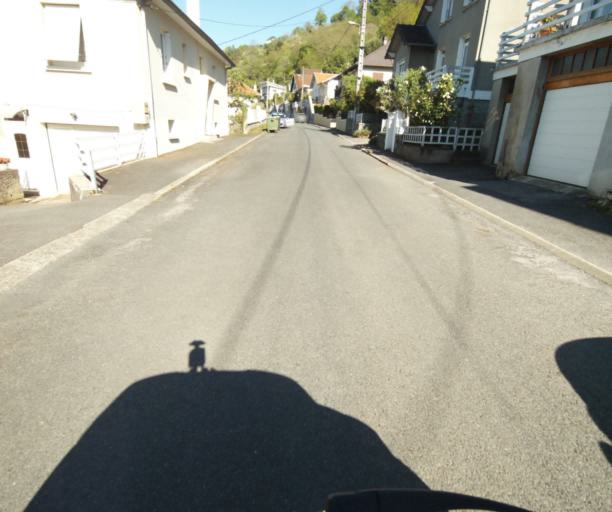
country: FR
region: Limousin
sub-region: Departement de la Correze
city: Tulle
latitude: 45.2771
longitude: 1.7779
